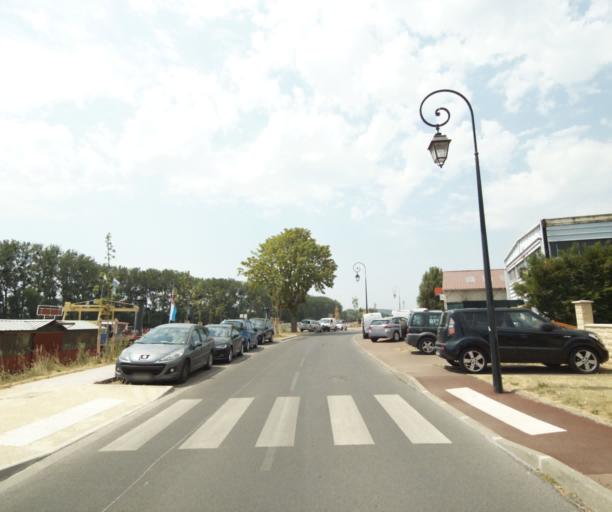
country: FR
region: Ile-de-France
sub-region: Departement des Yvelines
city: Conflans-Sainte-Honorine
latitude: 48.9915
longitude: 2.1122
